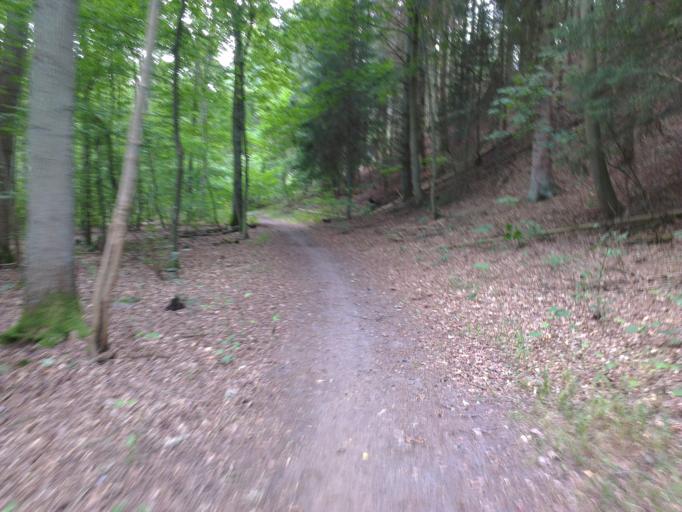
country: DK
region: Capital Region
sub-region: Frederikssund Kommune
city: Frederikssund
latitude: 55.8471
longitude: 12.0273
